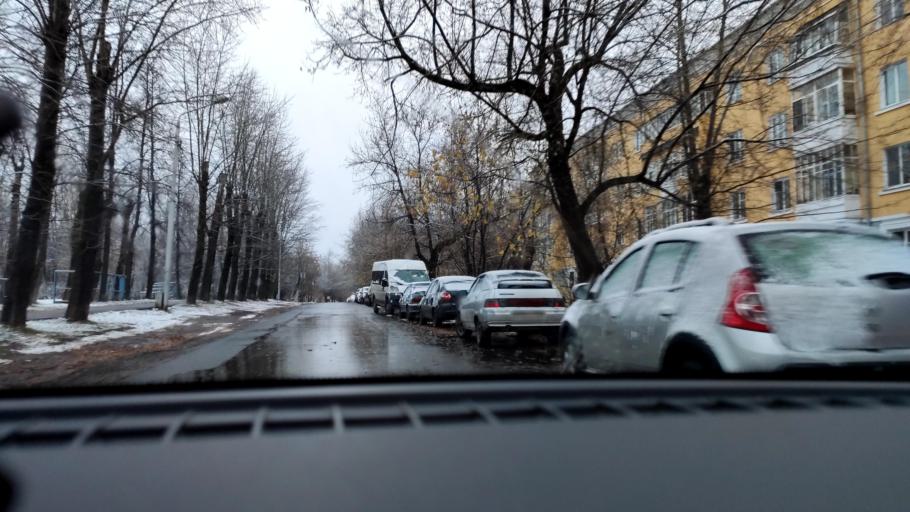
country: RU
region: Perm
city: Kultayevo
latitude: 57.9955
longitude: 55.9417
